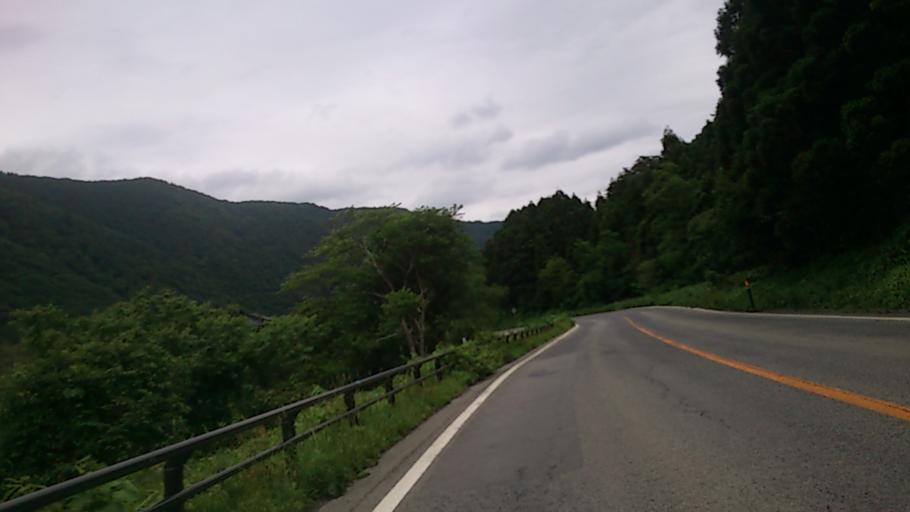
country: JP
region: Yamagata
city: Tsuruoka
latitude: 38.7680
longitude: 140.0437
